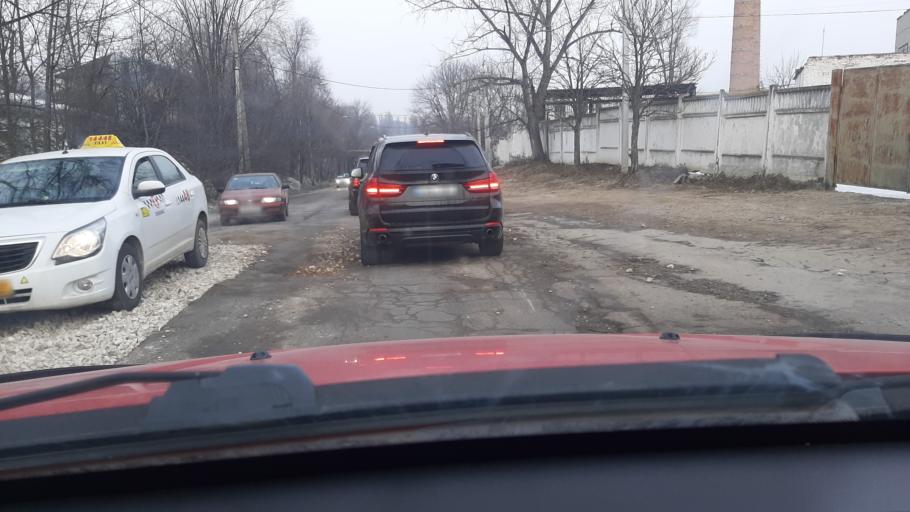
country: MD
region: Chisinau
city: Chisinau
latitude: 46.9778
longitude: 28.8917
